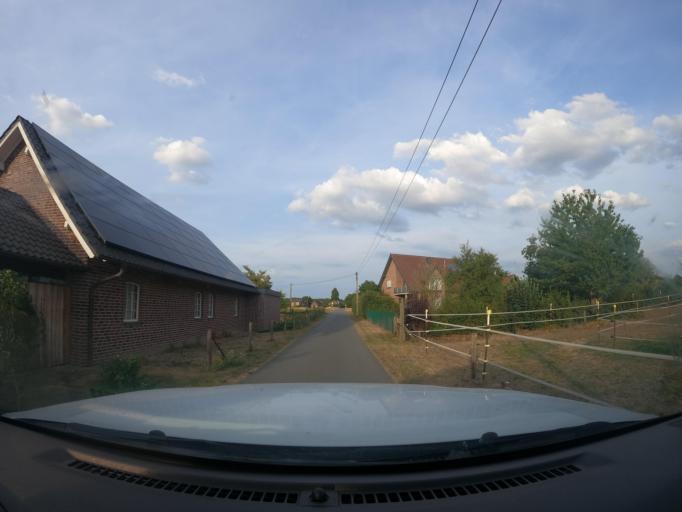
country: DE
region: North Rhine-Westphalia
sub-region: Regierungsbezirk Dusseldorf
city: Hamminkeln
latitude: 51.7216
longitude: 6.5824
